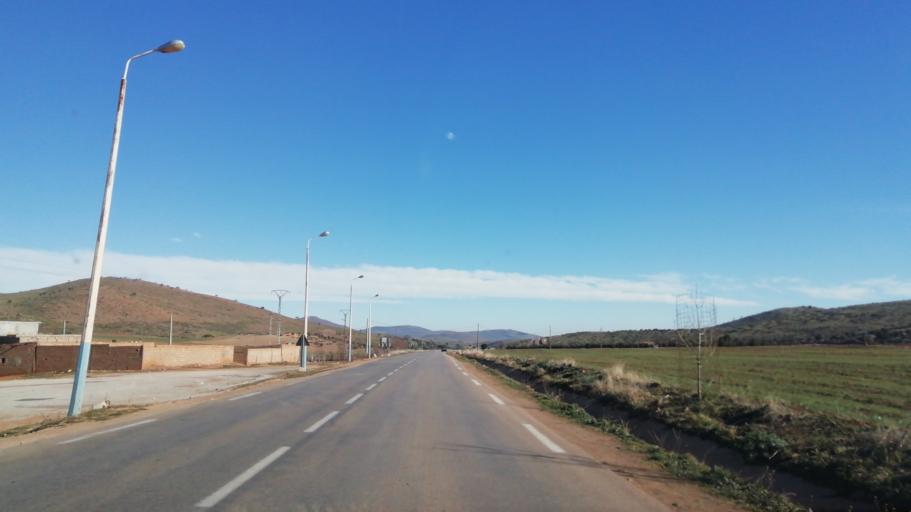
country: DZ
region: Tlemcen
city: Sebdou
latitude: 34.7437
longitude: -1.1660
